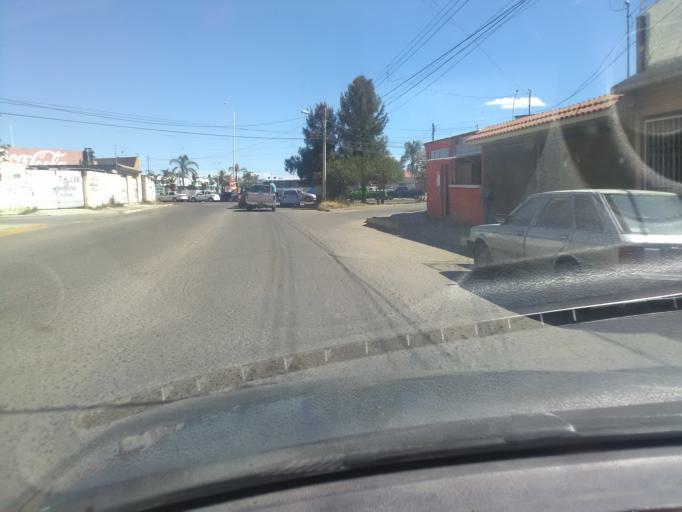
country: MX
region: Durango
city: Victoria de Durango
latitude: 24.0066
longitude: -104.6455
